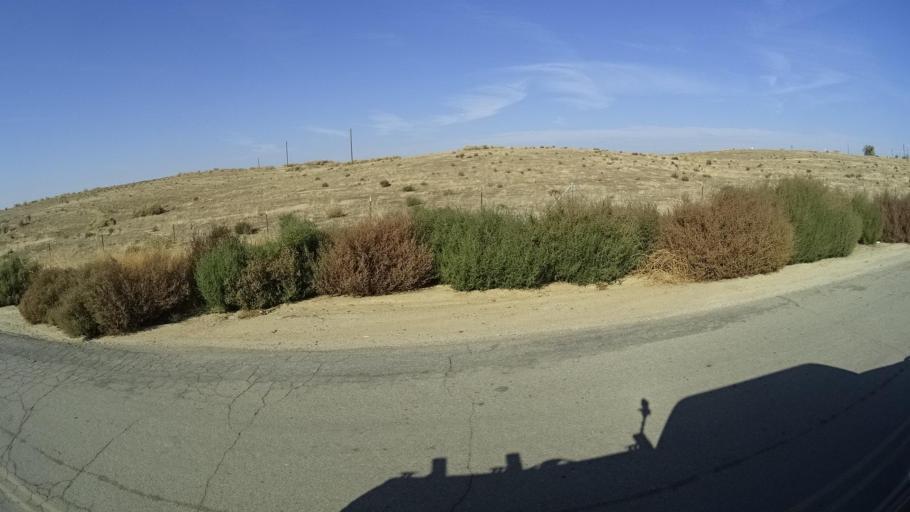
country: US
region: California
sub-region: Kern County
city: Oildale
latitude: 35.4909
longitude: -119.0426
